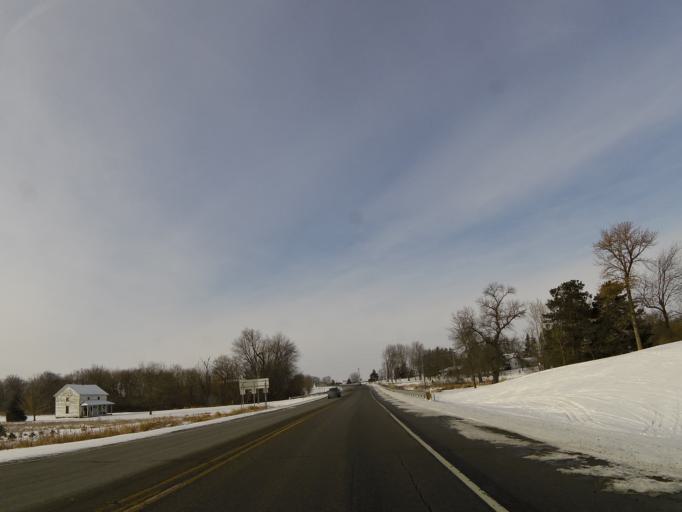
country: US
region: Minnesota
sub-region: McLeod County
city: Lester Prairie
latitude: 44.9055
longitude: -93.9742
